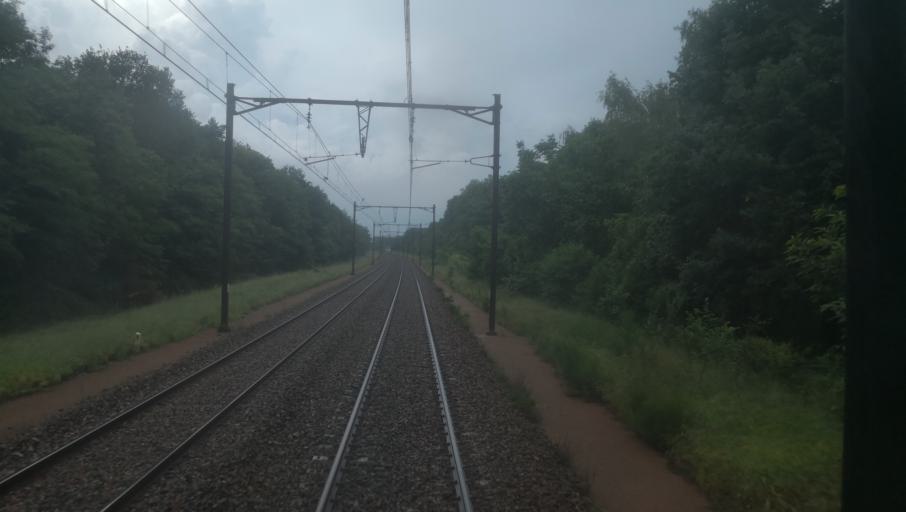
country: FR
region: Centre
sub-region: Departement du Loiret
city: Saint-Cyr-en-Val
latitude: 47.8219
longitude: 1.9481
